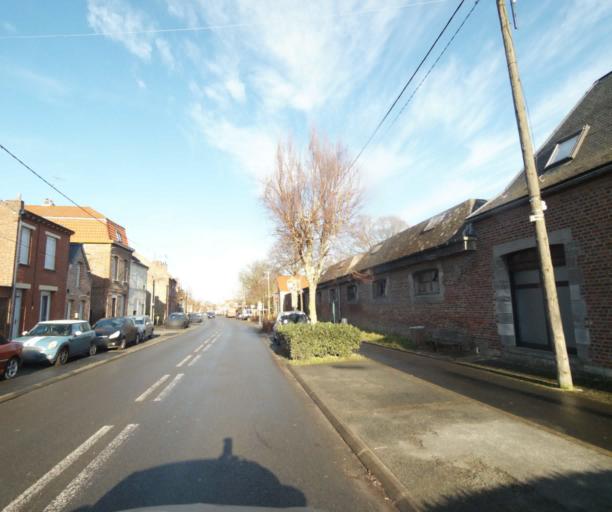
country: FR
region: Nord-Pas-de-Calais
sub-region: Departement du Nord
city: Famars
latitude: 50.3172
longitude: 3.5186
